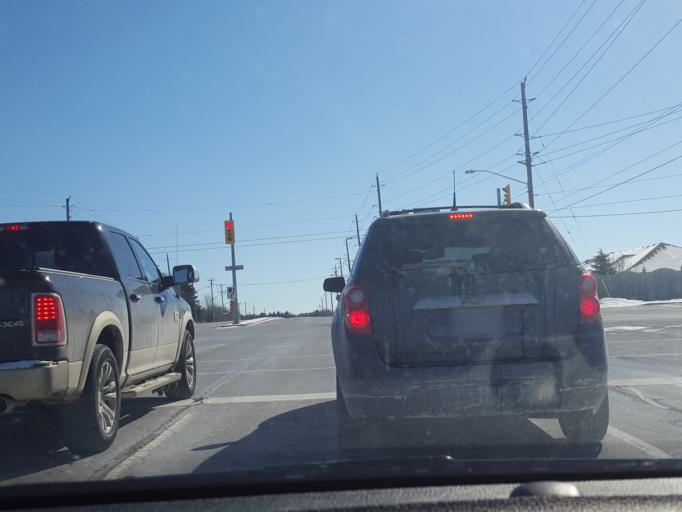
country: CA
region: Ontario
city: Waterloo
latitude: 43.4679
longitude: -80.5666
